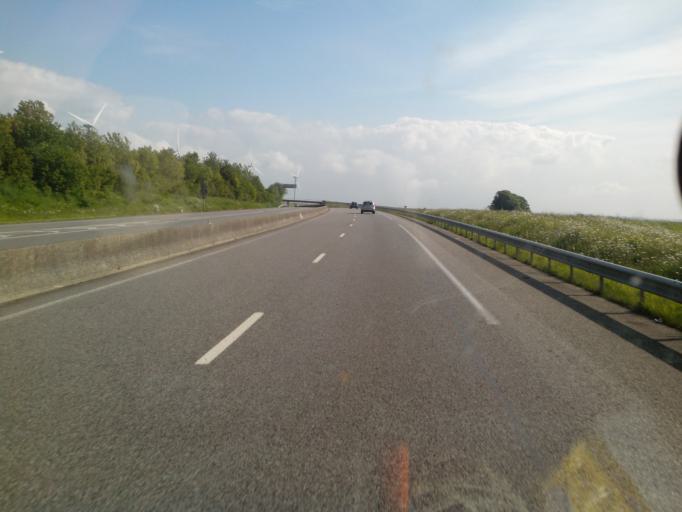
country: FR
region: Haute-Normandie
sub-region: Departement de la Seine-Maritime
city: Foucarmont
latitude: 49.8126
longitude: 1.5100
